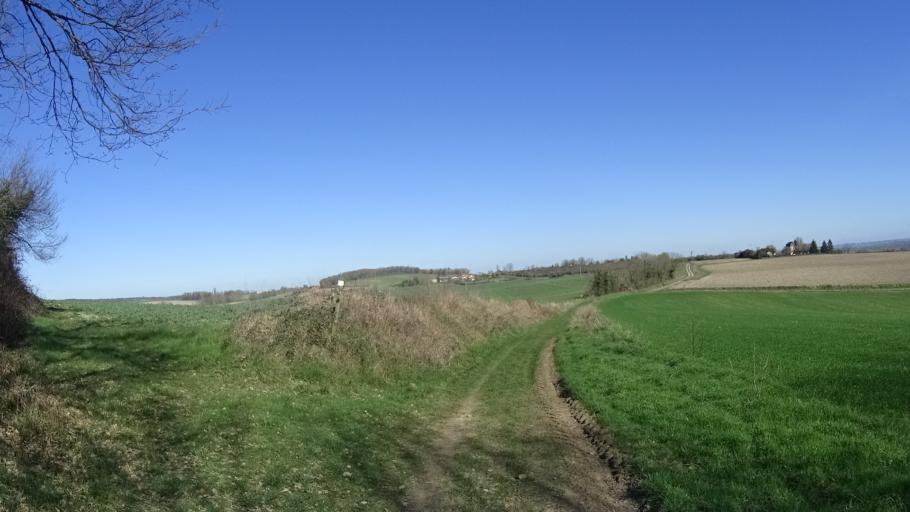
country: FR
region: Aquitaine
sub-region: Departement de la Dordogne
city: Saint-Aulaye
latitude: 45.2346
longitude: 0.1318
